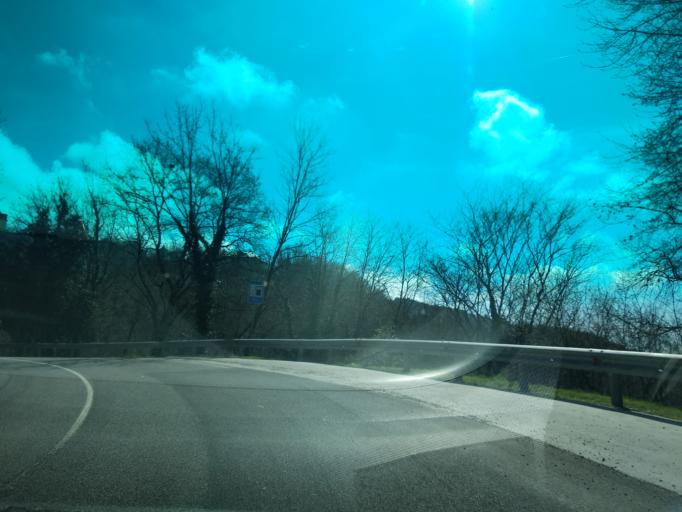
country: RU
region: Krasnodarskiy
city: Tuapse
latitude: 44.0916
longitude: 39.1176
